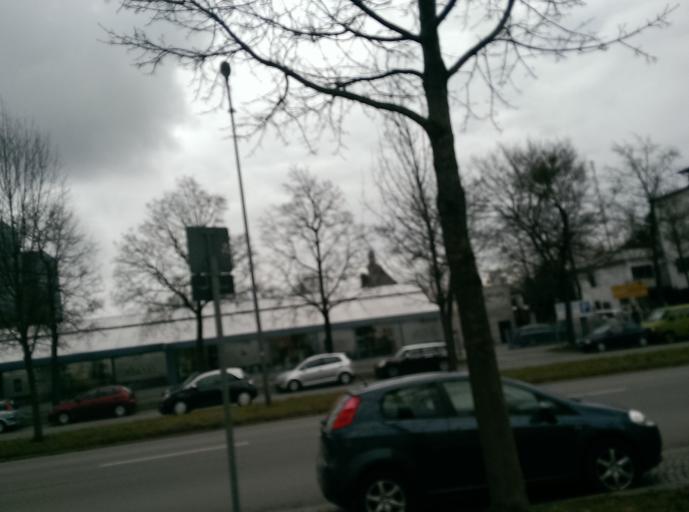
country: DE
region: Bavaria
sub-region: Upper Bavaria
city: Bogenhausen
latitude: 48.1752
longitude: 11.5996
